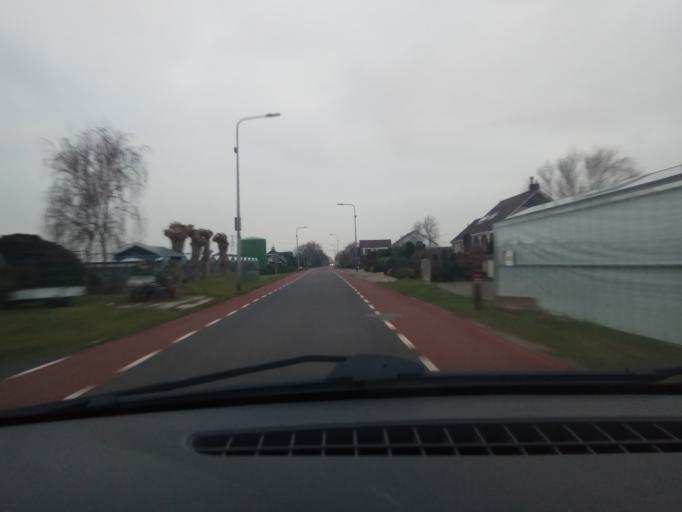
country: NL
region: South Holland
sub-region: Gemeente Westland
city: Maasdijk
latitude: 51.9623
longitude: 4.2048
